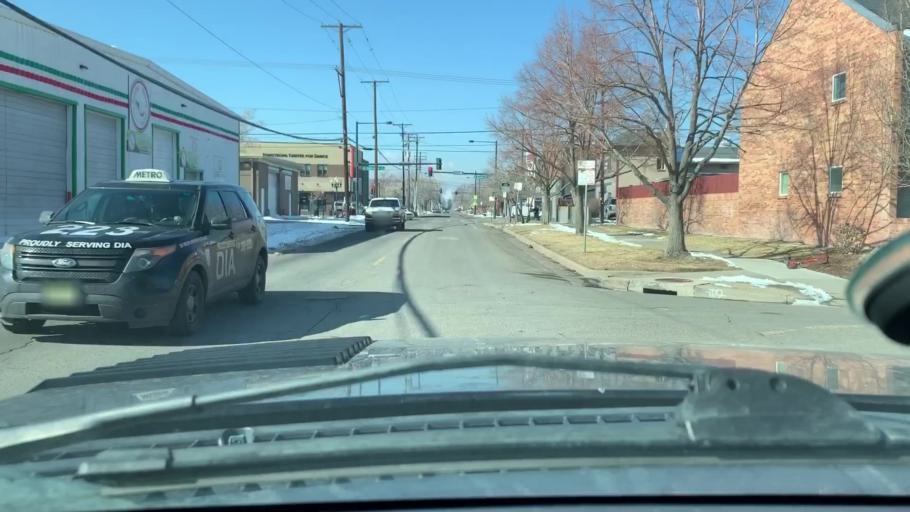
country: US
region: Colorado
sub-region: Denver County
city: Denver
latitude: 39.7337
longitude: -104.9976
